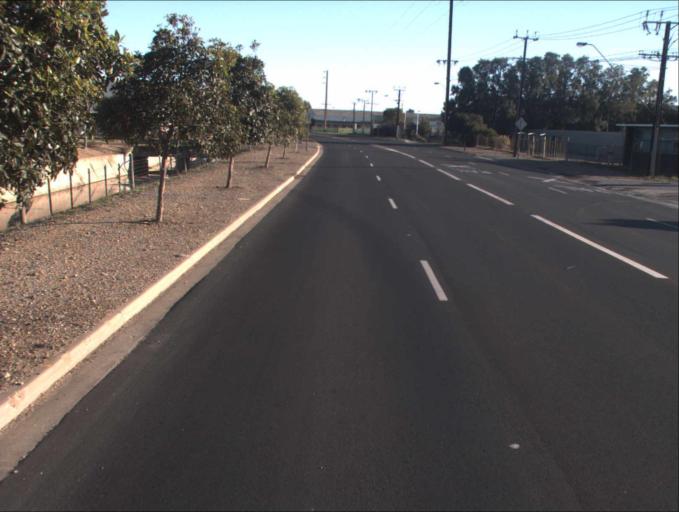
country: AU
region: South Australia
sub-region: Port Adelaide Enfield
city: Alberton
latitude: -34.8432
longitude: 138.5310
